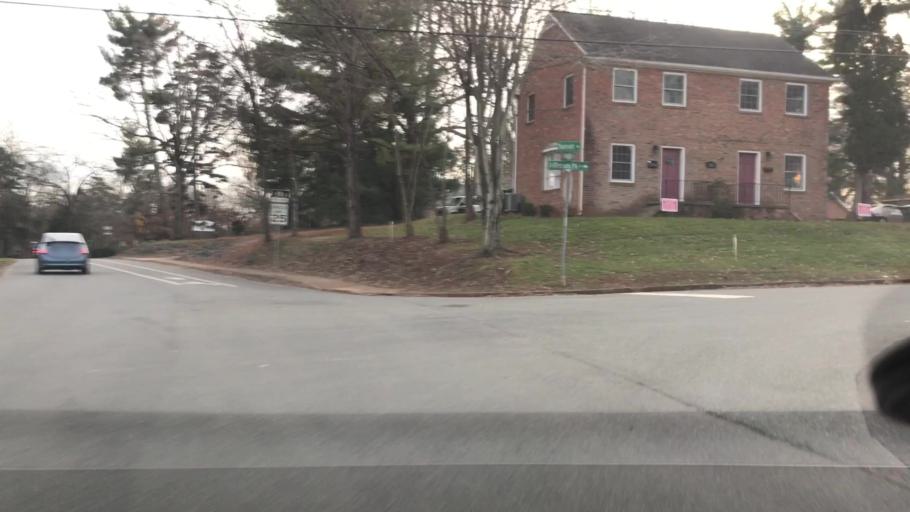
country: US
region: Virginia
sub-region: City of Charlottesville
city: Charlottesville
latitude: 38.0206
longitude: -78.5149
